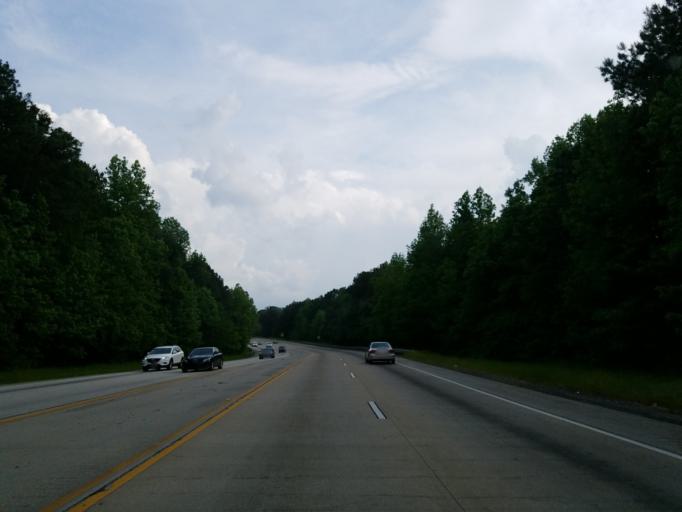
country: US
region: Georgia
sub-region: Douglas County
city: Lithia Springs
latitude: 33.8130
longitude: -84.6553
